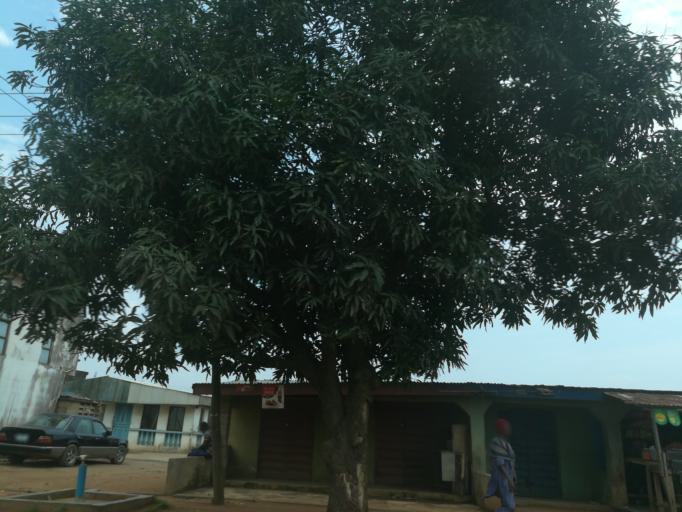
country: NG
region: Lagos
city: Ikorodu
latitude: 6.5756
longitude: 3.5922
